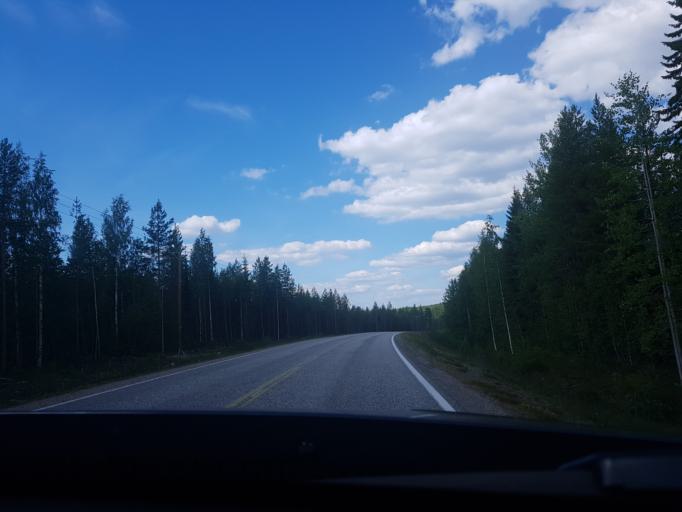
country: FI
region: Kainuu
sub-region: Kehys-Kainuu
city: Kuhmo
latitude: 64.2445
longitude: 29.8083
